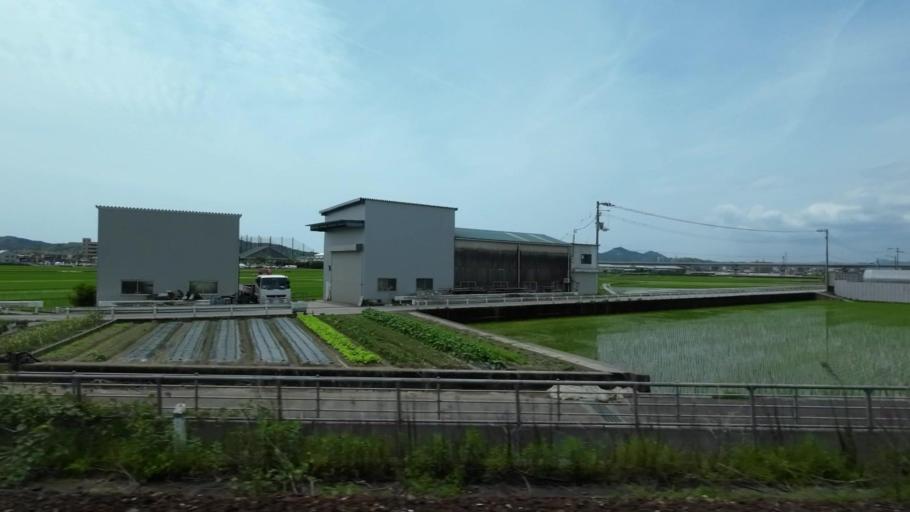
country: JP
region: Kochi
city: Kochi-shi
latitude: 33.5791
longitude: 133.5771
